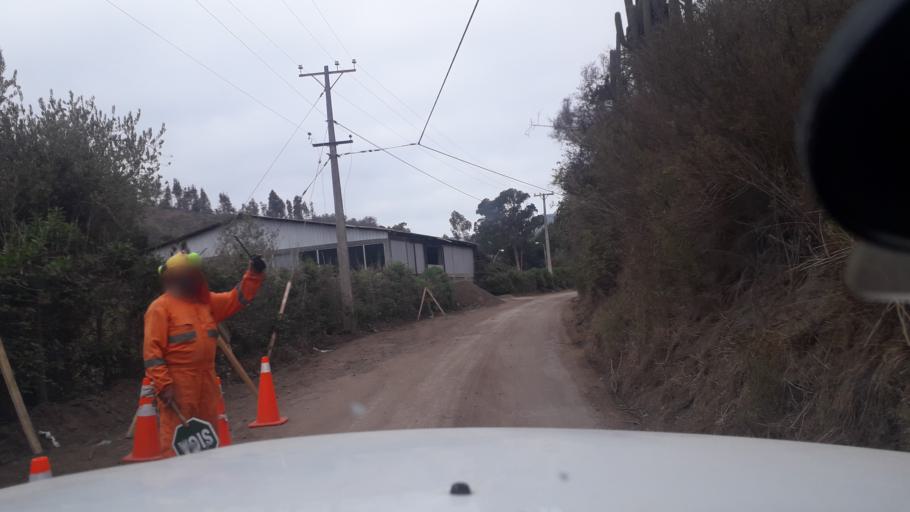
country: CL
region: Valparaiso
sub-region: Provincia de Valparaiso
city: Valparaiso
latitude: -33.1134
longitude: -71.6542
